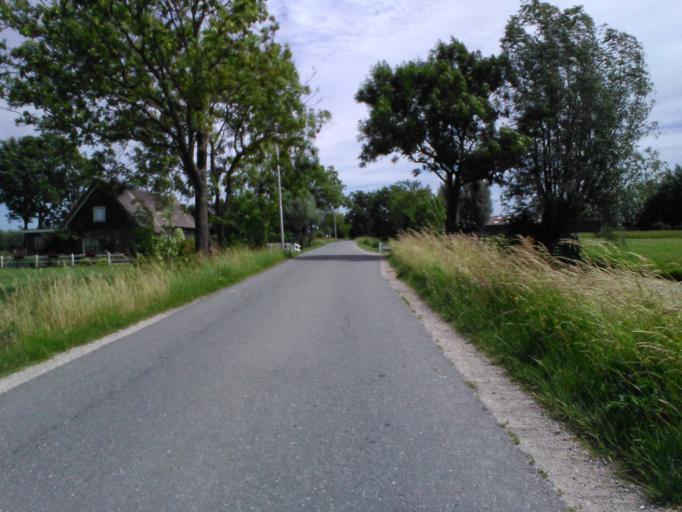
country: NL
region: South Holland
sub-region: Gemeente Sliedrecht
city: Sliedrecht
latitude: 51.8439
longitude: 4.7499
